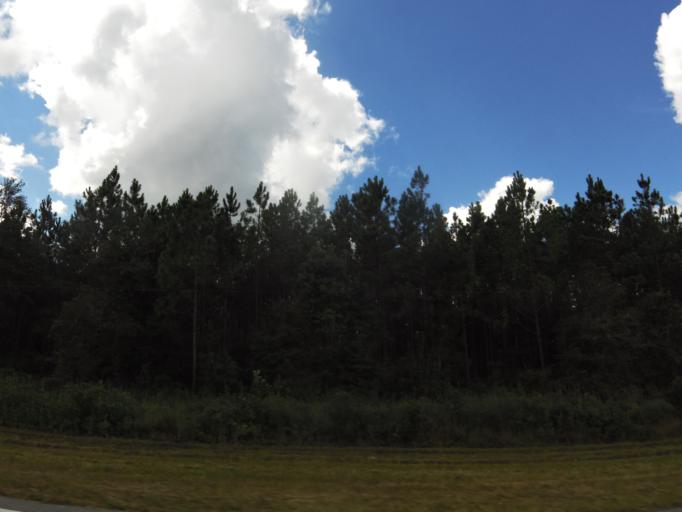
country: US
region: Georgia
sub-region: Charlton County
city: Folkston
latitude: 30.9230
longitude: -82.0207
